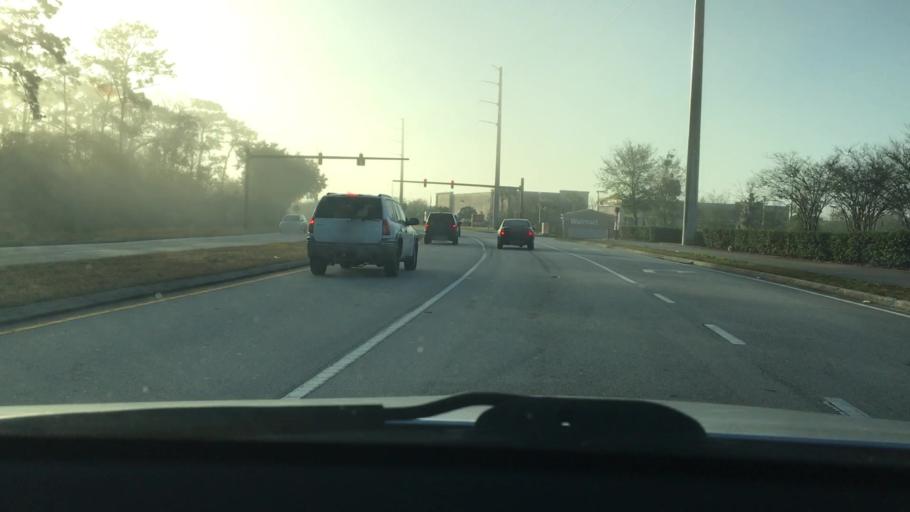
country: US
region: Florida
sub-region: Volusia County
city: Deltona
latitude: 28.8740
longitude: -81.1653
